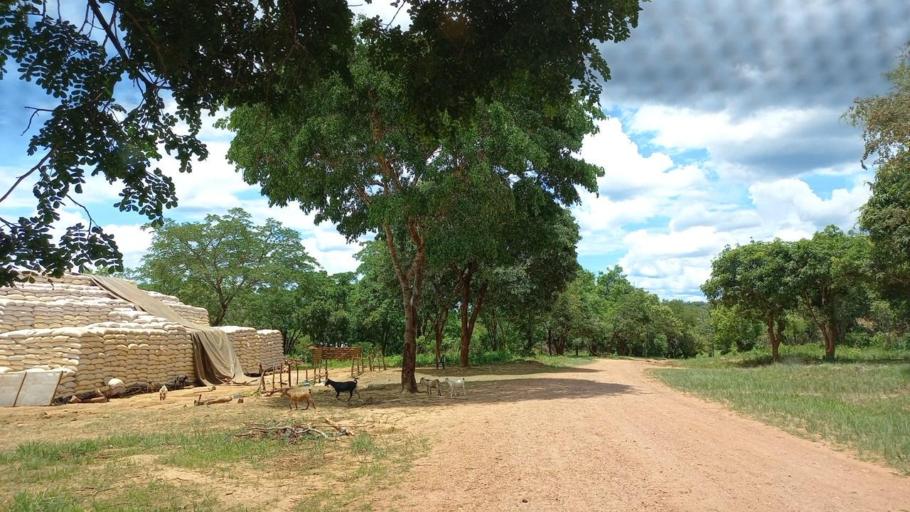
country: ZM
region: North-Western
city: Mwinilunga
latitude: -12.5463
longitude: 24.1999
